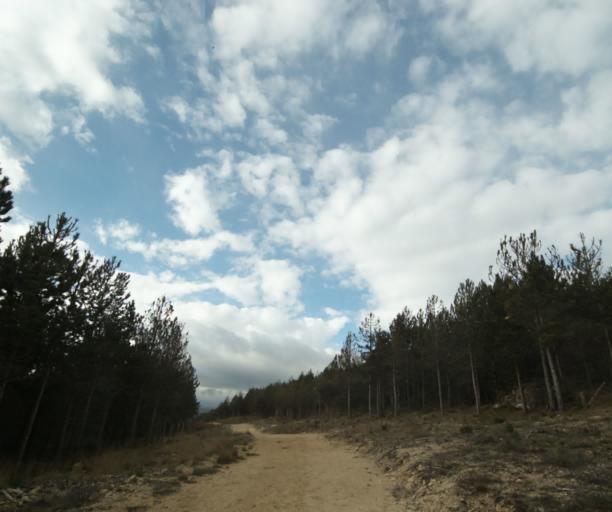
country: FR
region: Midi-Pyrenees
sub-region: Departement de l'Aveyron
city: Millau
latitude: 44.1197
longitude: 3.1516
